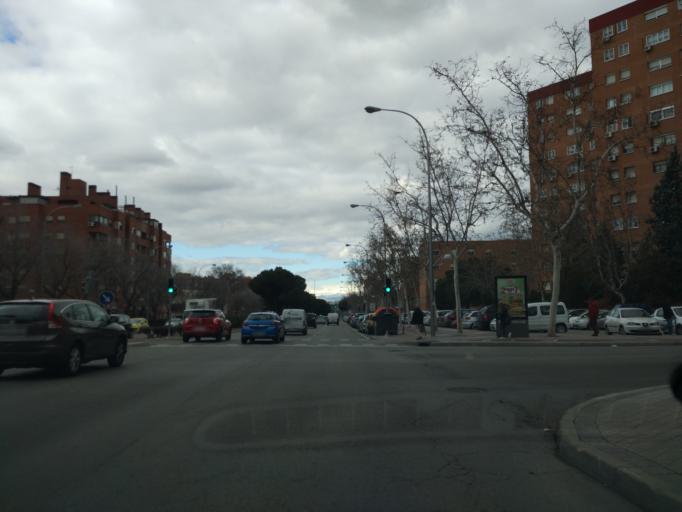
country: ES
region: Madrid
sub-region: Provincia de Madrid
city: San Blas
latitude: 40.4221
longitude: -3.6264
